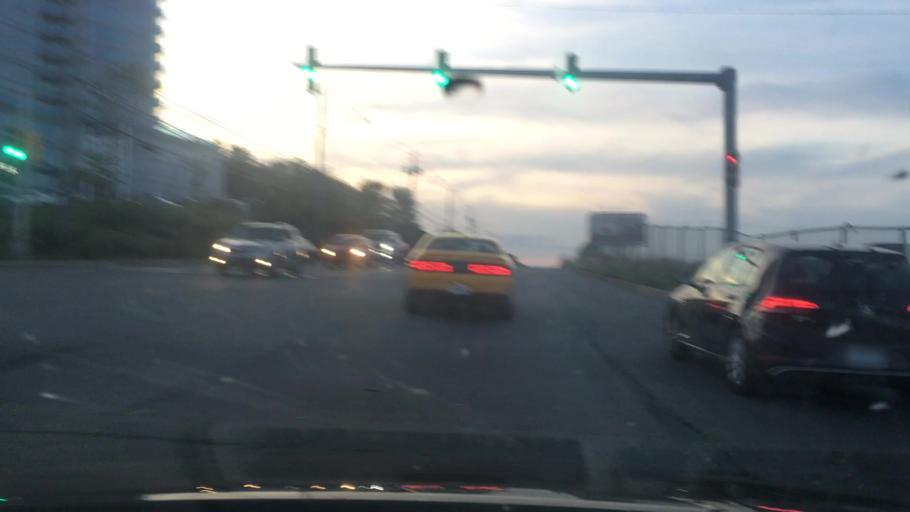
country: CA
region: Nova Scotia
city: Dartmouth
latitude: 44.6643
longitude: -63.6342
